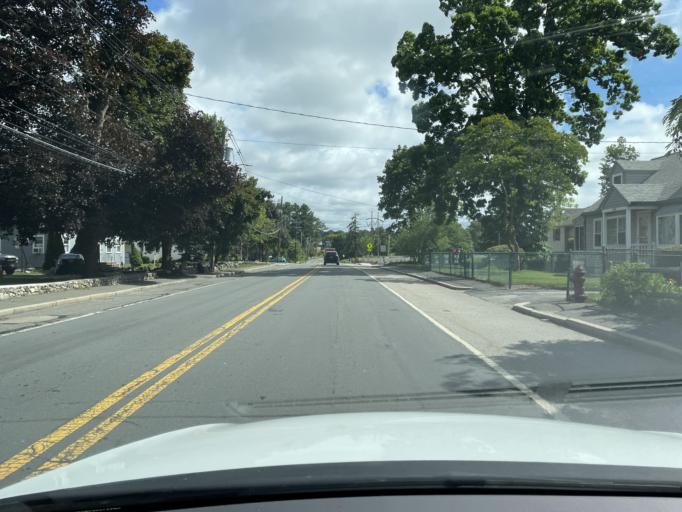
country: US
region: Massachusetts
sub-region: Middlesex County
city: Woburn
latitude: 42.4697
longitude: -71.1768
